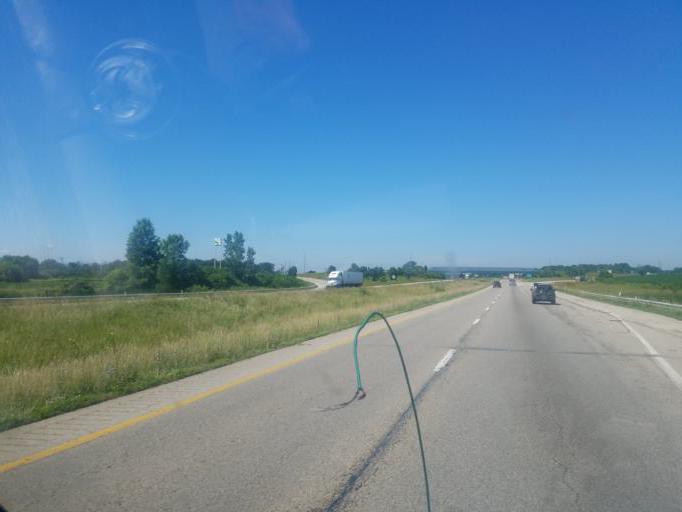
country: US
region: Ohio
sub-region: Clinton County
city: Wilmington
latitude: 39.4876
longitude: -83.9374
